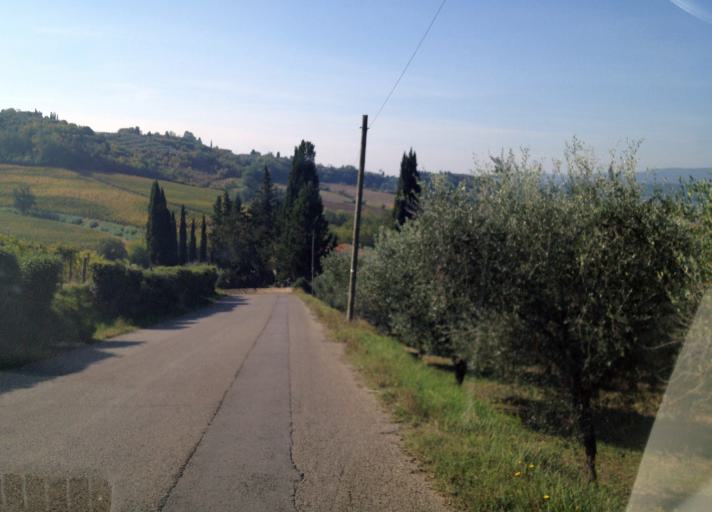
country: IT
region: Tuscany
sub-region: Provincia di Siena
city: Poggibonsi
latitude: 43.4908
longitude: 11.1783
